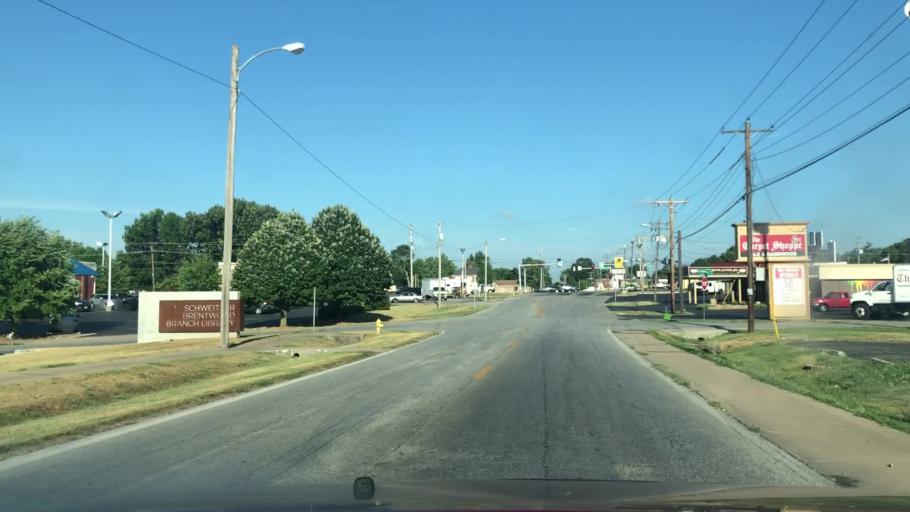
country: US
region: Missouri
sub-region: Greene County
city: Springfield
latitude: 37.1742
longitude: -93.2606
